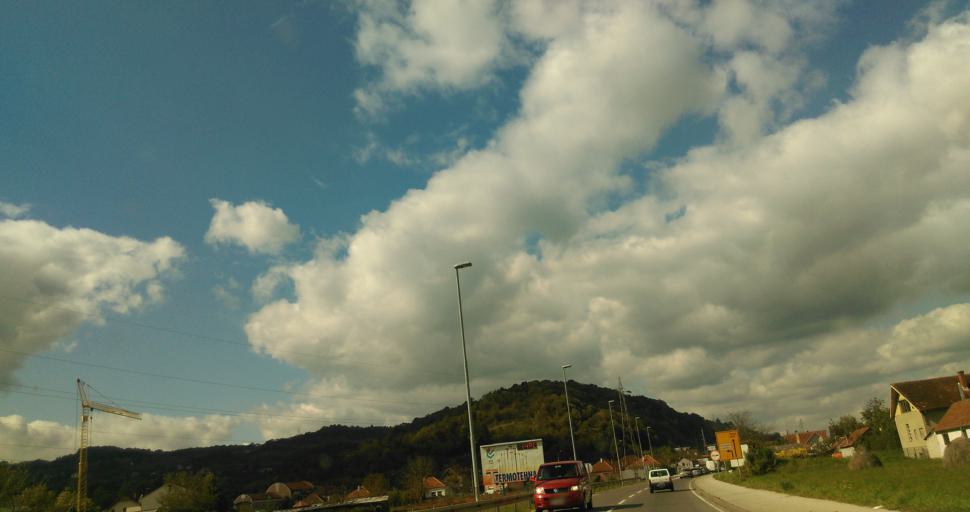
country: RS
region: Central Serbia
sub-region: Moravicki Okrug
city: Cacak
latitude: 43.8820
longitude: 20.3228
